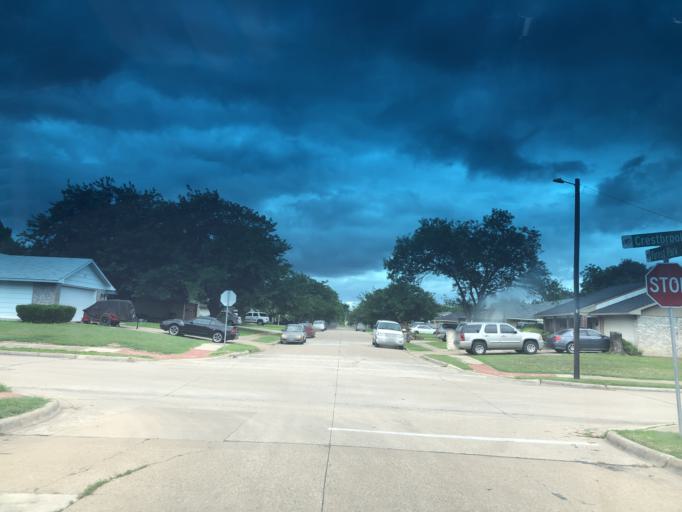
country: US
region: Texas
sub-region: Dallas County
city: Grand Prairie
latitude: 32.7026
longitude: -97.0120
